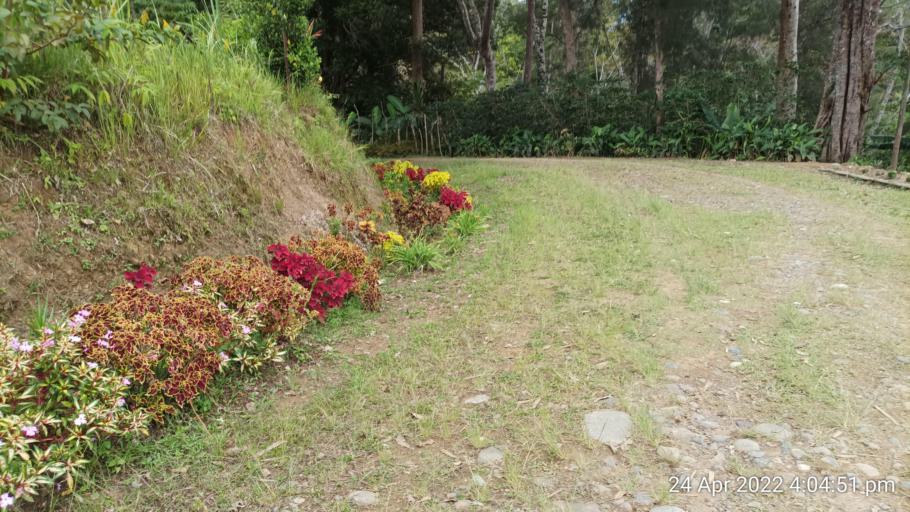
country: PG
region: Jiwaka
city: Minj
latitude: -5.9026
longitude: 144.8224
